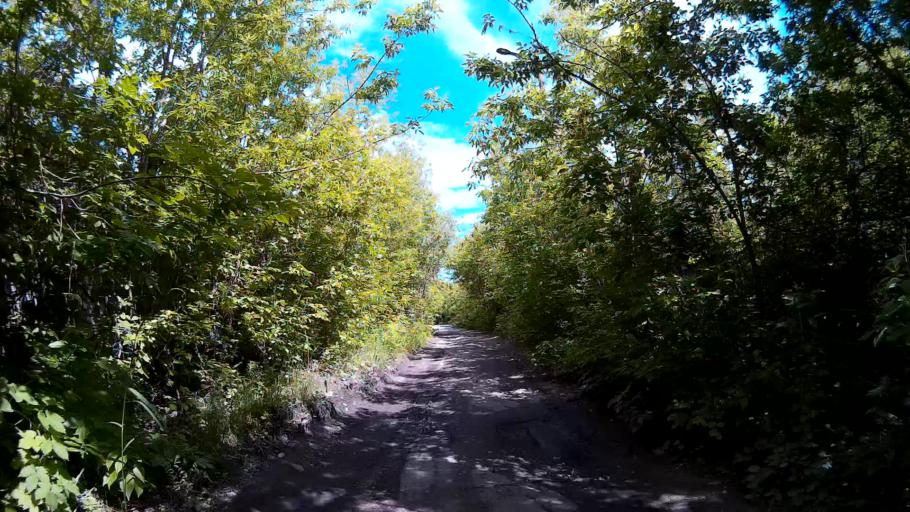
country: RU
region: Ulyanovsk
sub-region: Ulyanovskiy Rayon
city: Ulyanovsk
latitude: 54.2803
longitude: 48.3597
